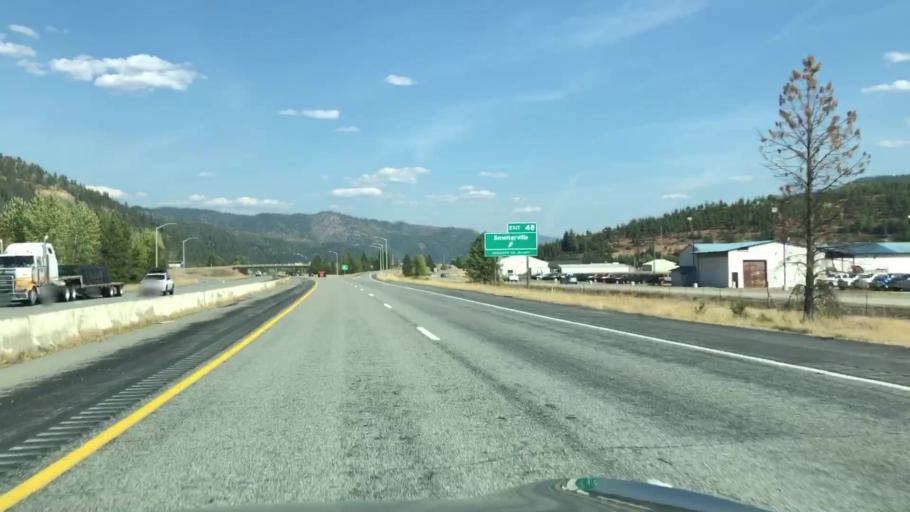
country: US
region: Idaho
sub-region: Shoshone County
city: Pinehurst
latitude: 47.5461
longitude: -116.1826
